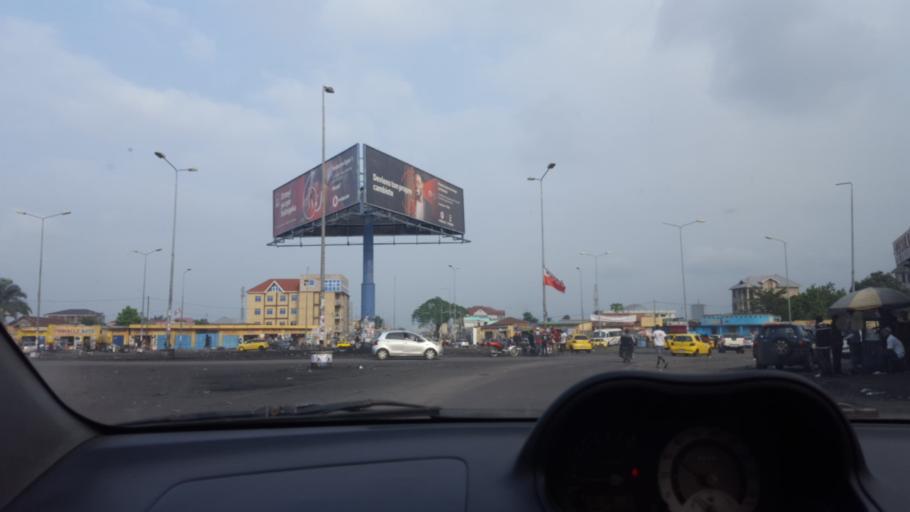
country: CD
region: Kinshasa
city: Kinshasa
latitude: -4.3398
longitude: 15.3102
